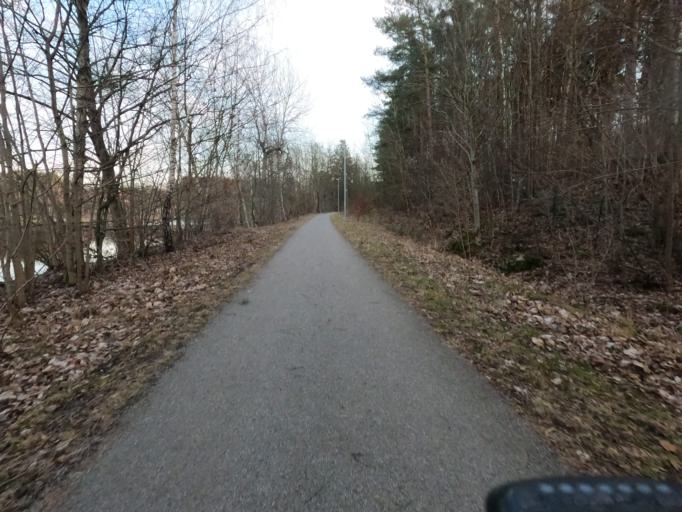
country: SE
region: Blekinge
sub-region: Karlshamns Kommun
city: Svangsta
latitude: 56.2547
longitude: 14.7851
